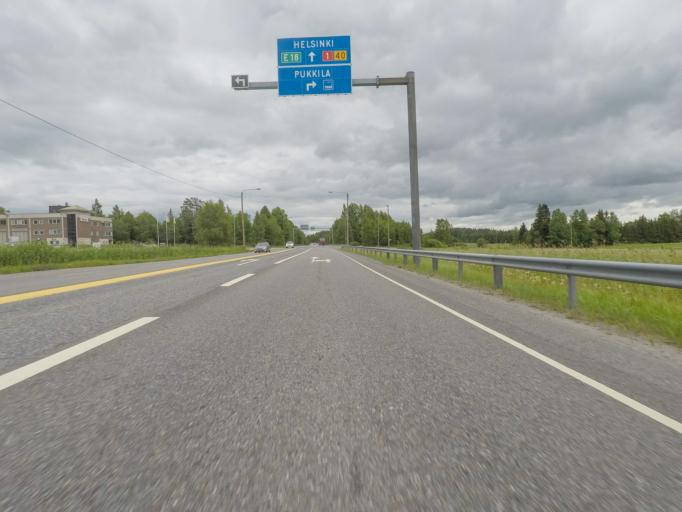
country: FI
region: Varsinais-Suomi
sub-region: Turku
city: Lieto
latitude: 60.4511
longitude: 22.4579
